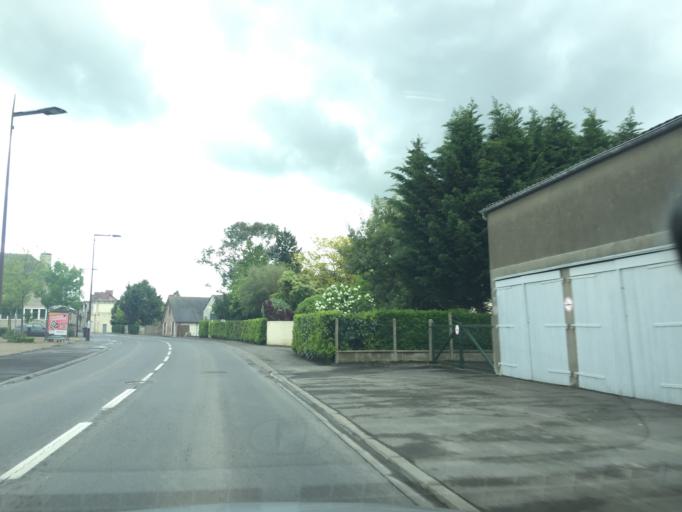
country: FR
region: Lower Normandy
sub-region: Departement de la Manche
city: Pontorson
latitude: 48.5557
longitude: -1.5119
